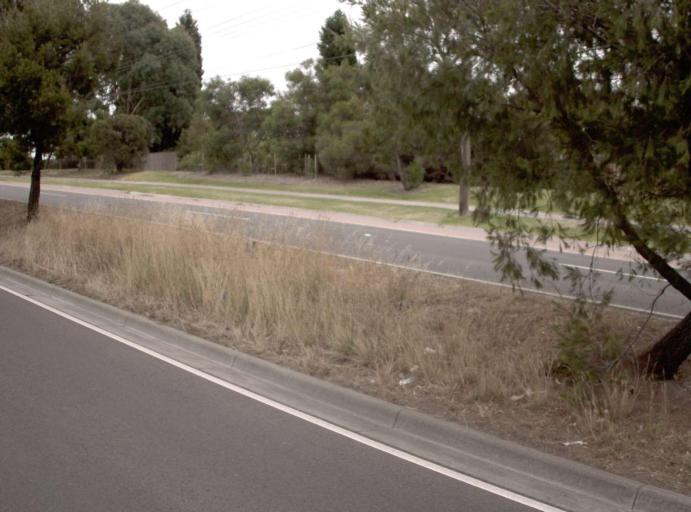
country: AU
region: Victoria
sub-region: Knox
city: Wantirna South
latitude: -37.8806
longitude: 145.2330
